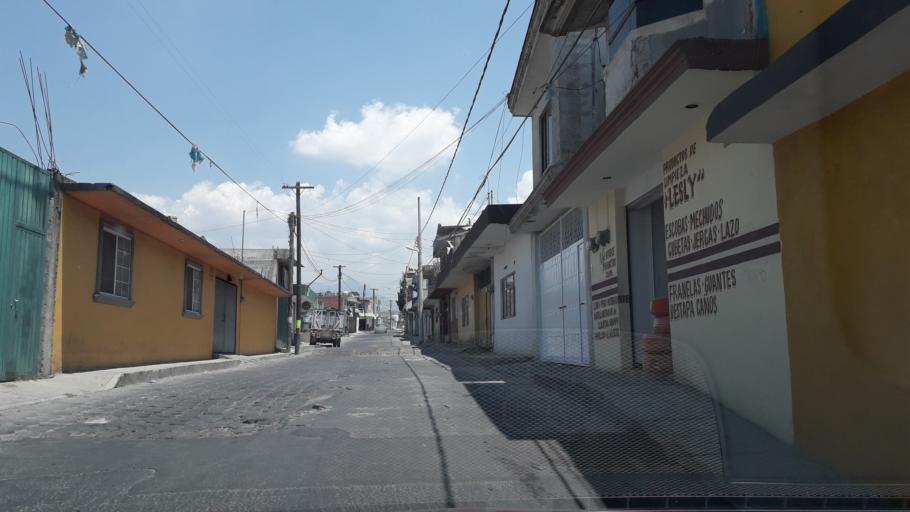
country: MX
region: Puebla
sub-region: Puebla
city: Santa Maria Xonacatepec
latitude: 19.0854
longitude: -98.1039
